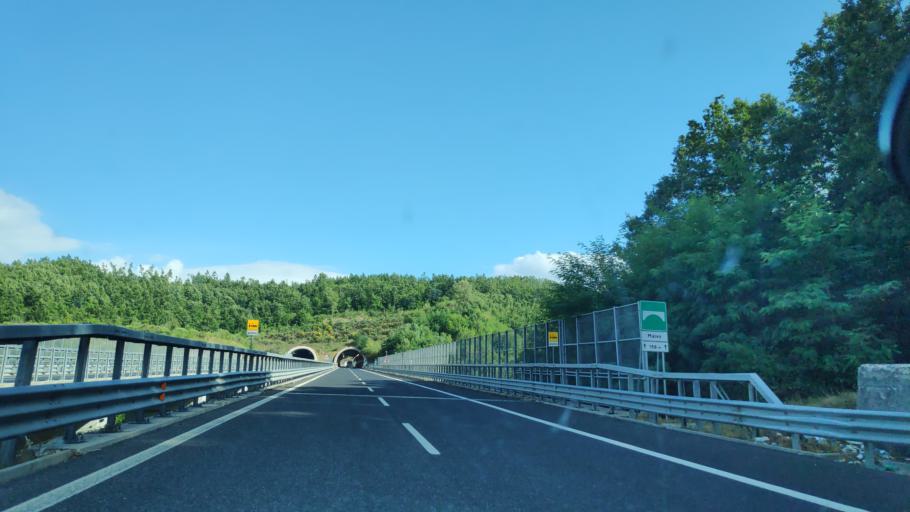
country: IT
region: Campania
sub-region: Provincia di Salerno
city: Casalbuono
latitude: 40.2357
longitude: 15.6624
